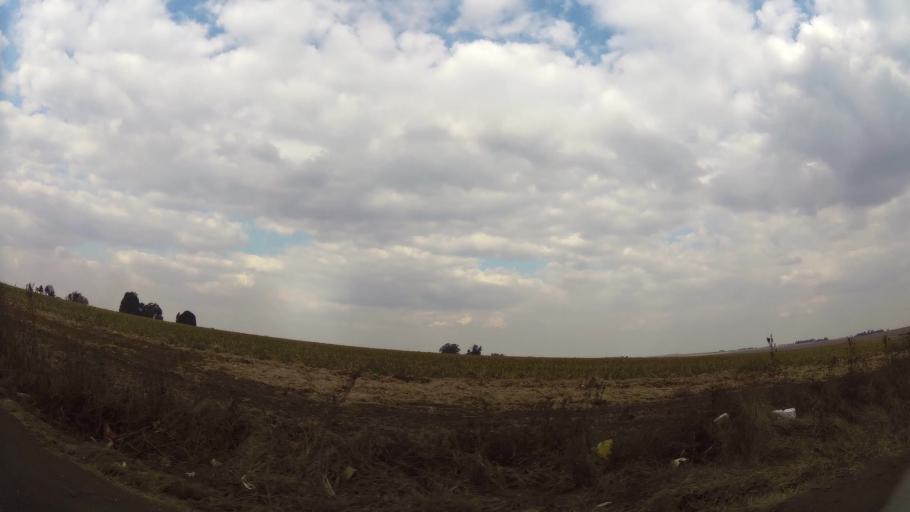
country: ZA
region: Mpumalanga
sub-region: Nkangala District Municipality
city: Delmas
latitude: -26.2626
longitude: 28.6311
